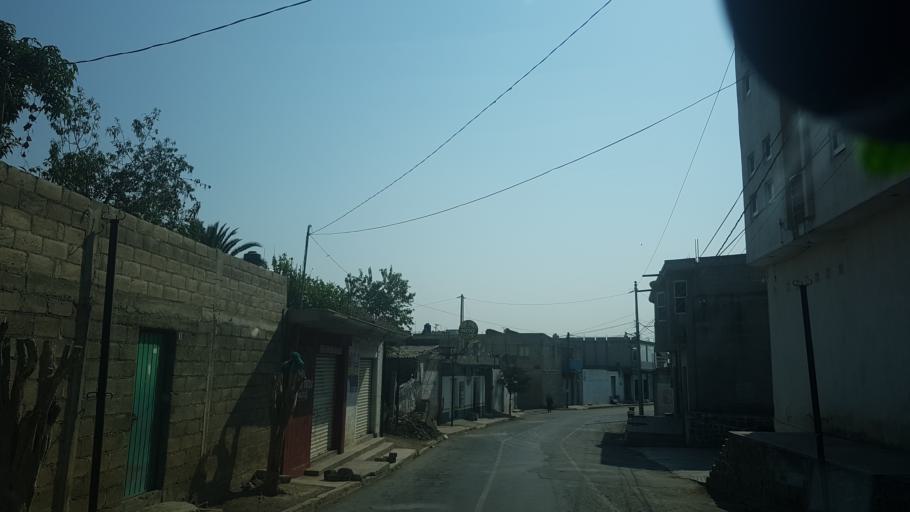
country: MX
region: Puebla
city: Nealtican
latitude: 19.0515
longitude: -98.4267
